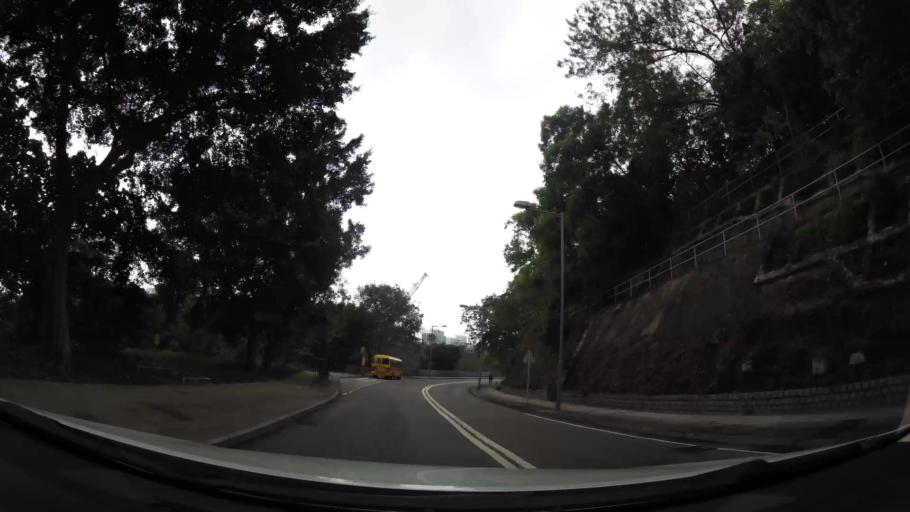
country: HK
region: Central and Western
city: Central
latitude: 22.2639
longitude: 114.1319
